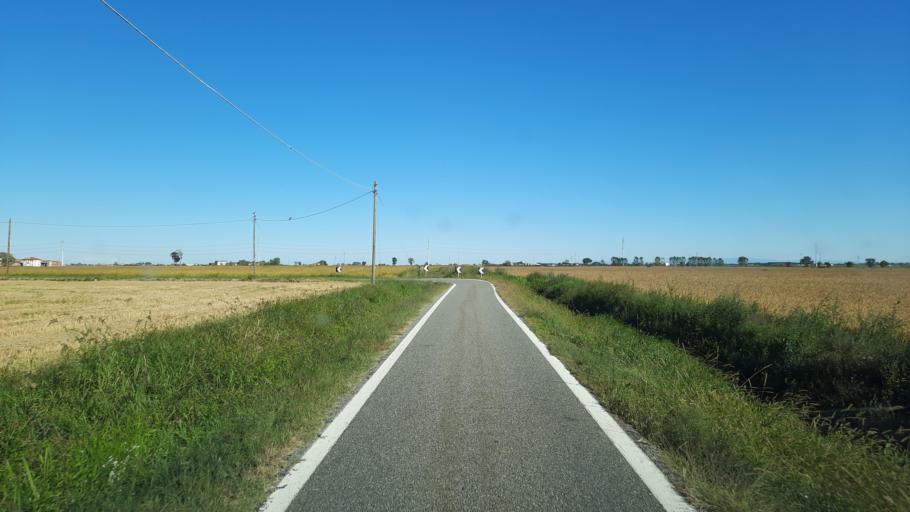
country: IT
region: Piedmont
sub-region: Provincia di Vercelli
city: Ronsecco
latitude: 45.2624
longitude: 8.2879
